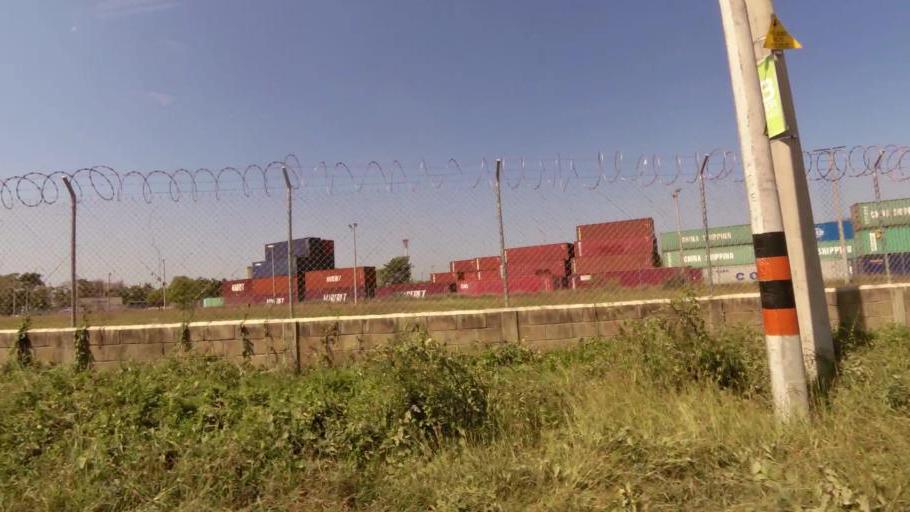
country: CO
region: Bolivar
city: Cartagena
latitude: 10.3538
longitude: -75.4887
